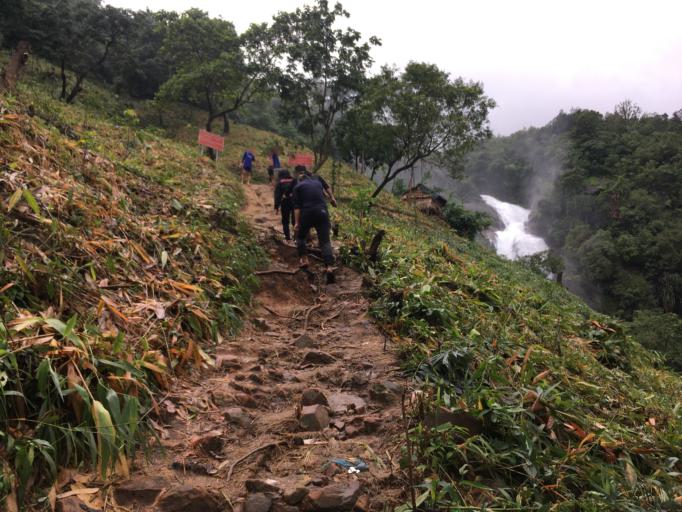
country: MM
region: Mon
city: Martaban
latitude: 16.6692
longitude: 97.5087
